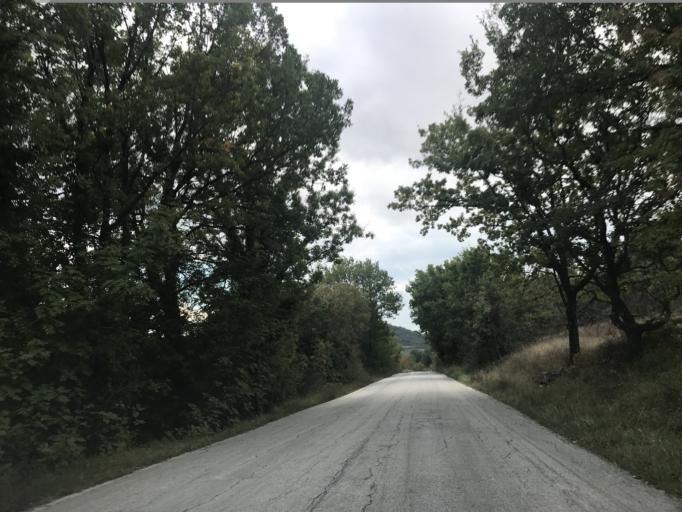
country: IT
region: Molise
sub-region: Provincia di Campobasso
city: Duronia
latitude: 41.6785
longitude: 14.4533
